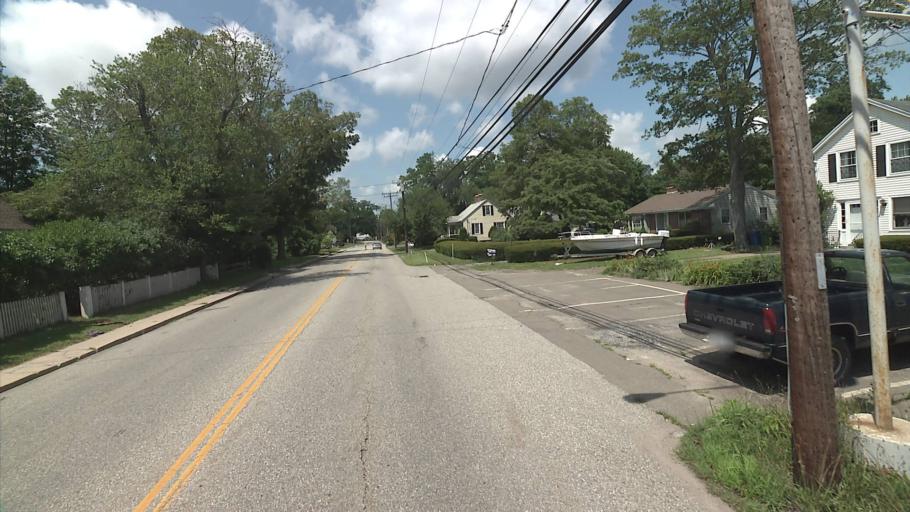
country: US
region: Connecticut
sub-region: Middlesex County
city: Essex Village
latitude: 41.3518
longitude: -72.4073
